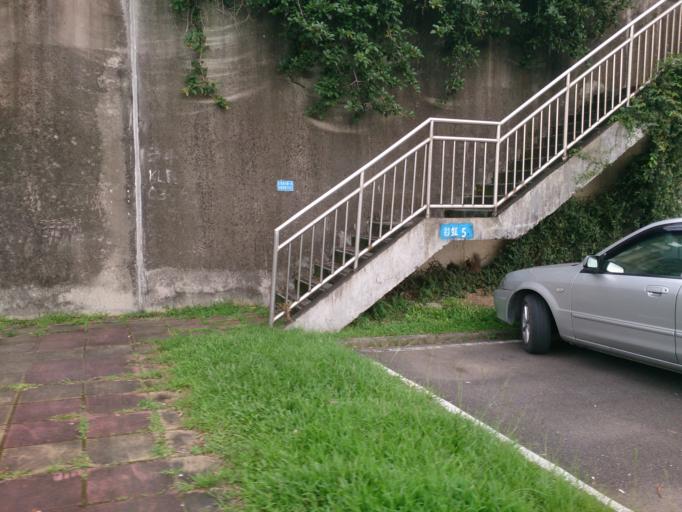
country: TW
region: Taipei
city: Taipei
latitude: 25.0639
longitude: 121.5722
